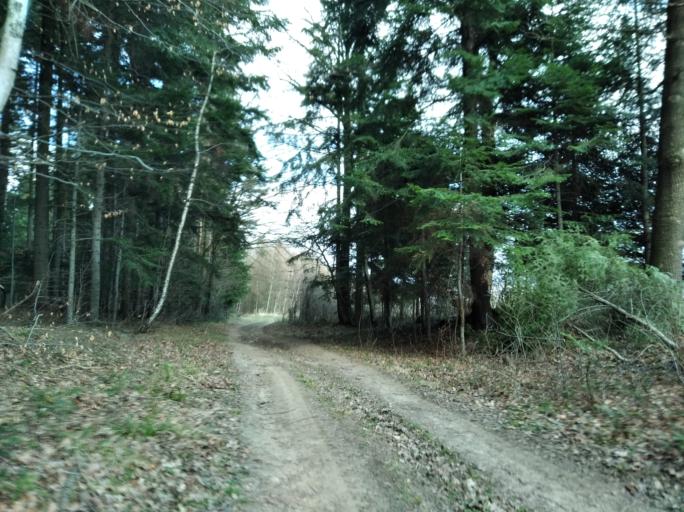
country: PL
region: Subcarpathian Voivodeship
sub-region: Powiat strzyzowski
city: Strzyzow
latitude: 49.8286
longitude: 21.8054
